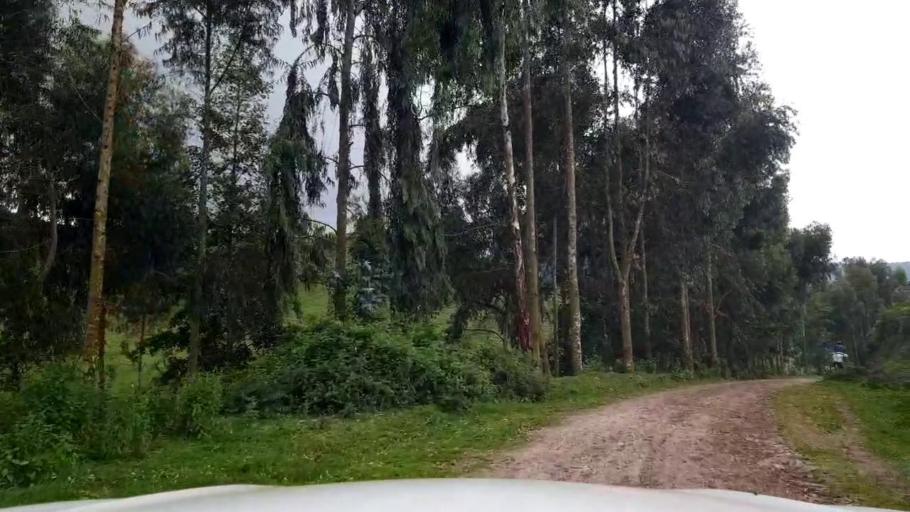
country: RW
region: Western Province
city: Gisenyi
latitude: -1.6866
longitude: 29.4201
